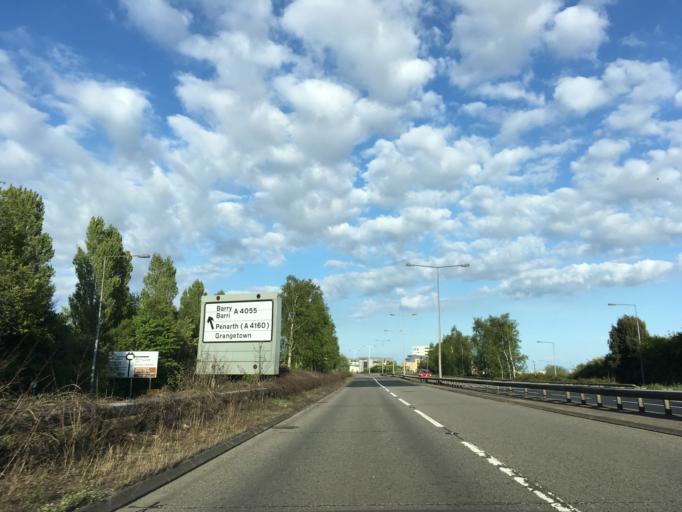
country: GB
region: Wales
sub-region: Vale of Glamorgan
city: Penarth
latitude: 51.4538
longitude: -3.1888
